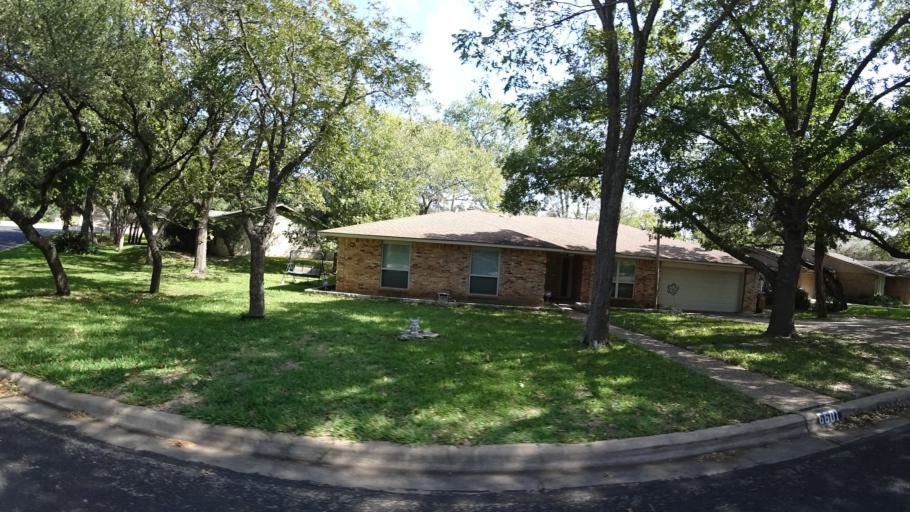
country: US
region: Texas
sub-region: Travis County
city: West Lake Hills
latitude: 30.3523
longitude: -97.7625
